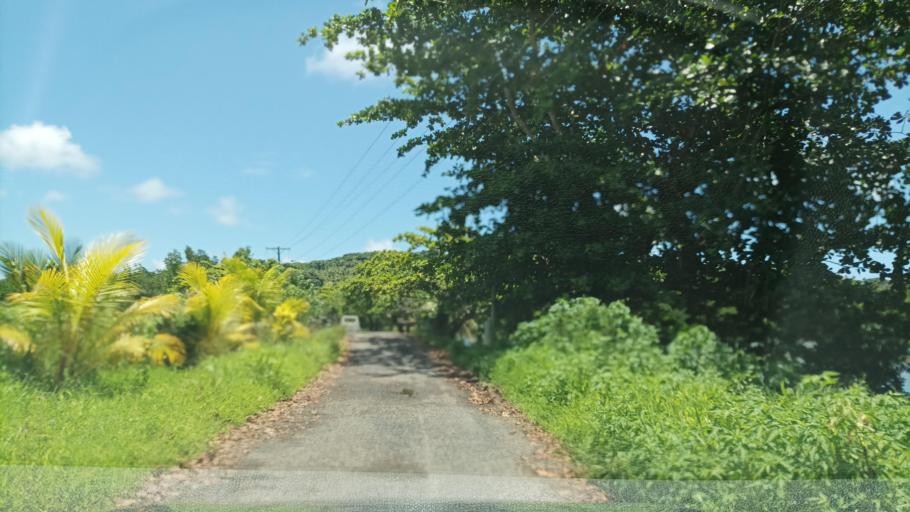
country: FM
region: Pohnpei
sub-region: Madolenihm Municipality
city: Madolenihm Municipality Government
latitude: 6.8435
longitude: 158.3131
